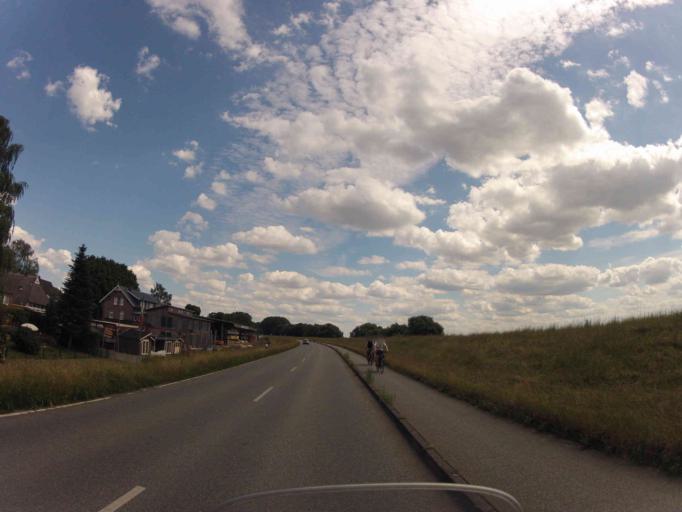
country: DE
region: Lower Saxony
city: Stelle
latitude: 53.4025
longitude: 10.1640
